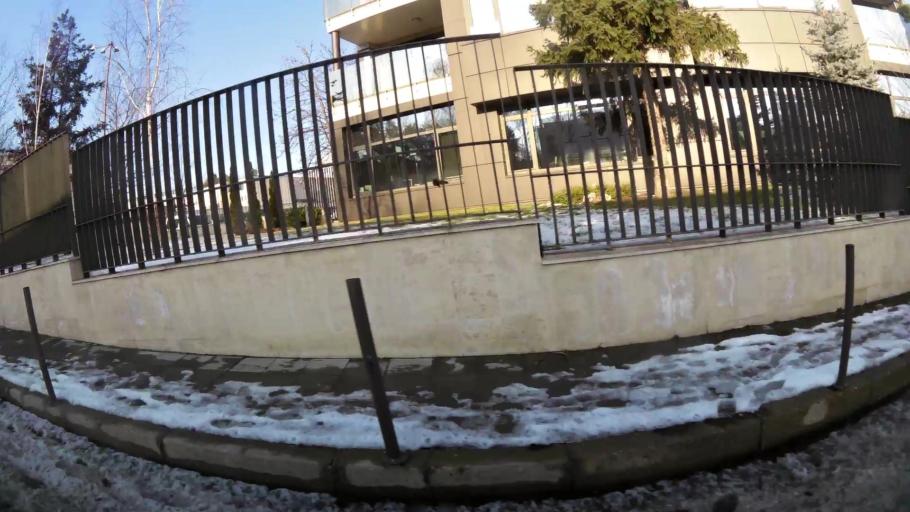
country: BG
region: Sofia-Capital
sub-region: Stolichna Obshtina
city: Sofia
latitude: 42.6713
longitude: 23.3466
